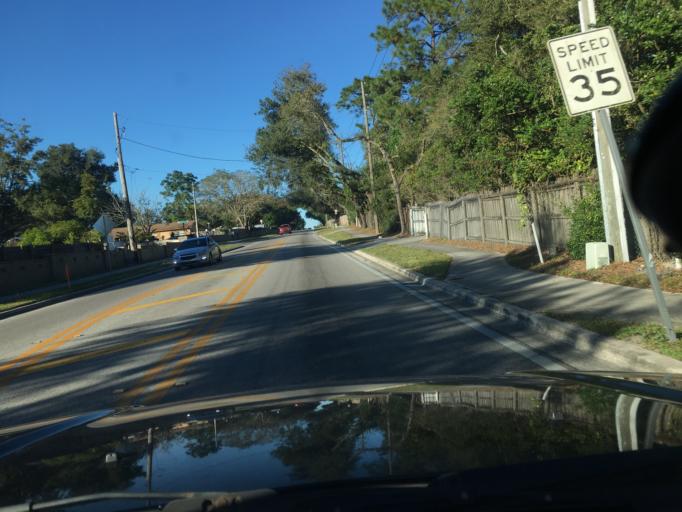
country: US
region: Florida
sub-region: Orange County
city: Pine Hills
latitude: 28.5895
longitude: -81.4678
